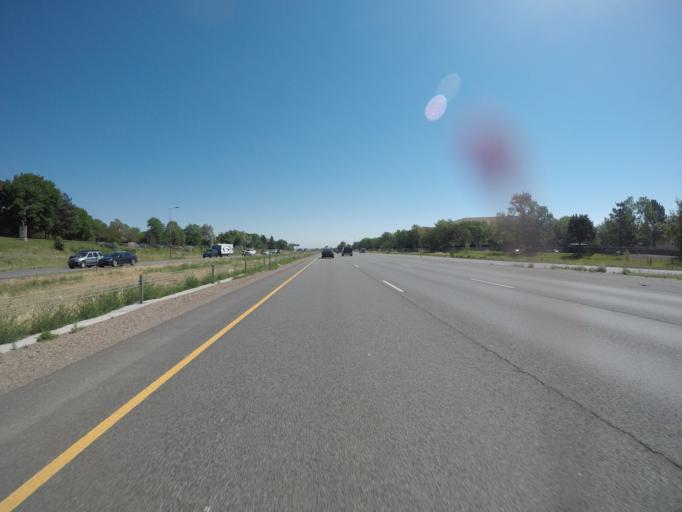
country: US
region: Colorado
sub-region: Jefferson County
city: Applewood
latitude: 39.7415
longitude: -105.1571
